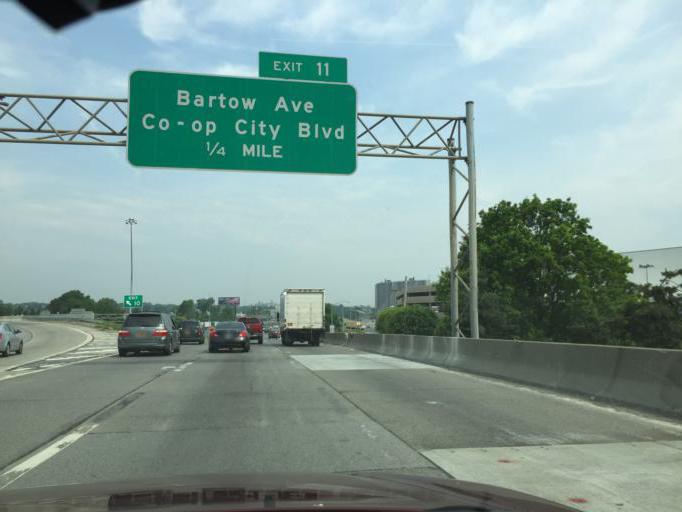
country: US
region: New York
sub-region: Bronx
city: Eastchester
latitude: 40.8615
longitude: -73.8284
